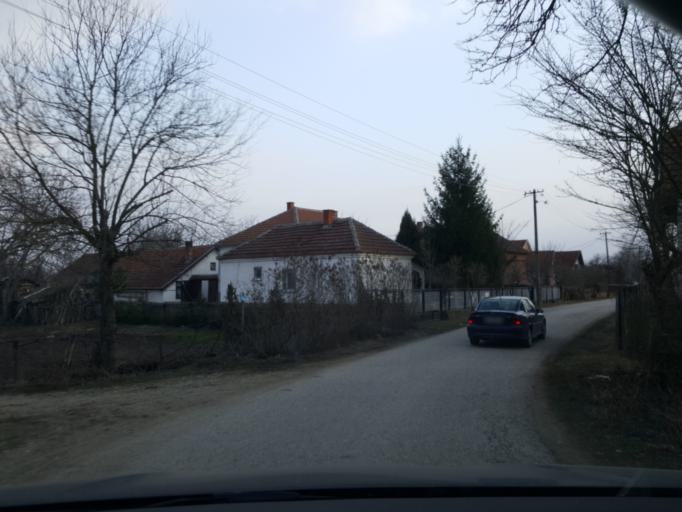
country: RS
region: Central Serbia
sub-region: Nisavski Okrug
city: Aleksinac
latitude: 43.5773
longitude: 21.6464
